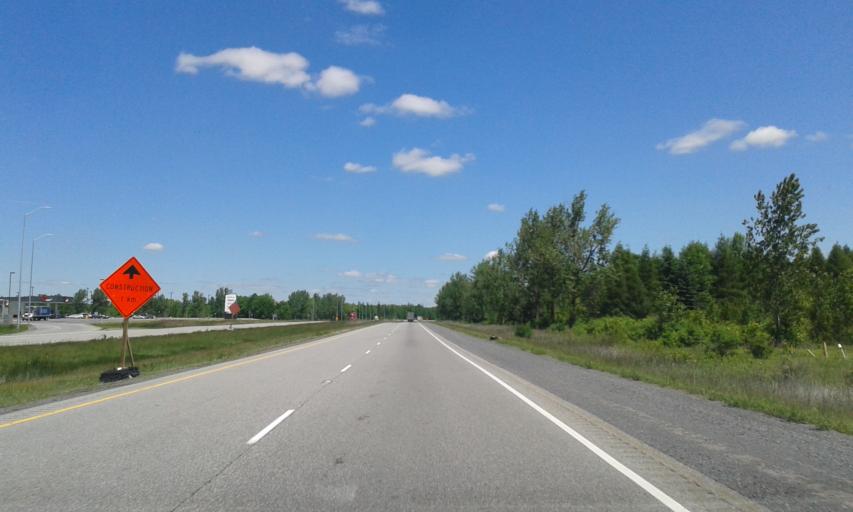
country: US
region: New York
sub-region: St. Lawrence County
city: Norfolk
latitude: 44.9677
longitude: -75.0807
